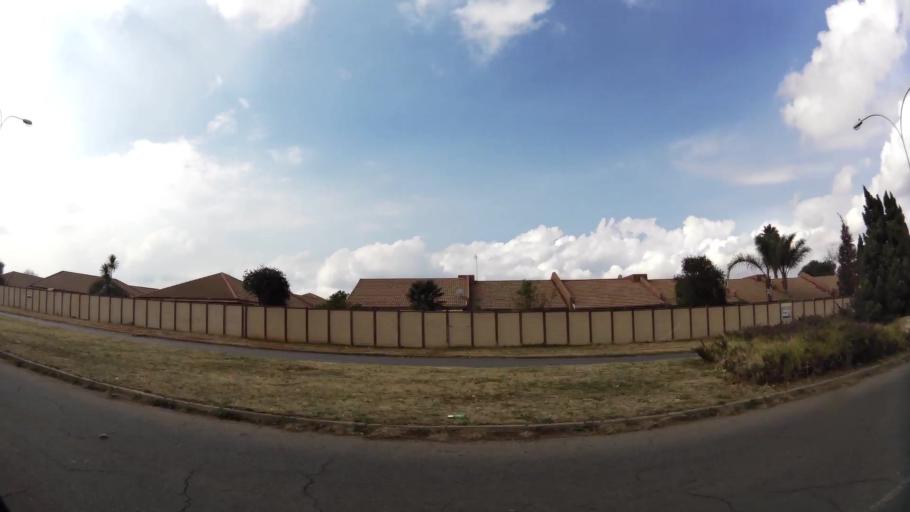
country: ZA
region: Gauteng
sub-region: Sedibeng District Municipality
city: Vanderbijlpark
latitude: -26.7240
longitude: 27.8370
